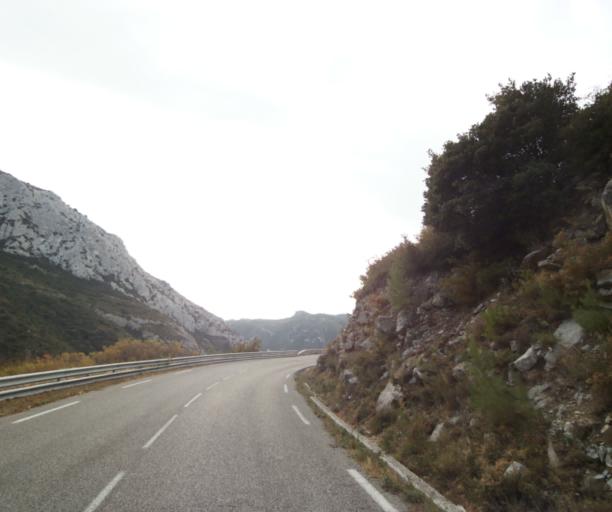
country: FR
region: Provence-Alpes-Cote d'Azur
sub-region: Departement des Bouches-du-Rhone
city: Gemenos
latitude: 43.3013
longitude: 5.6631
